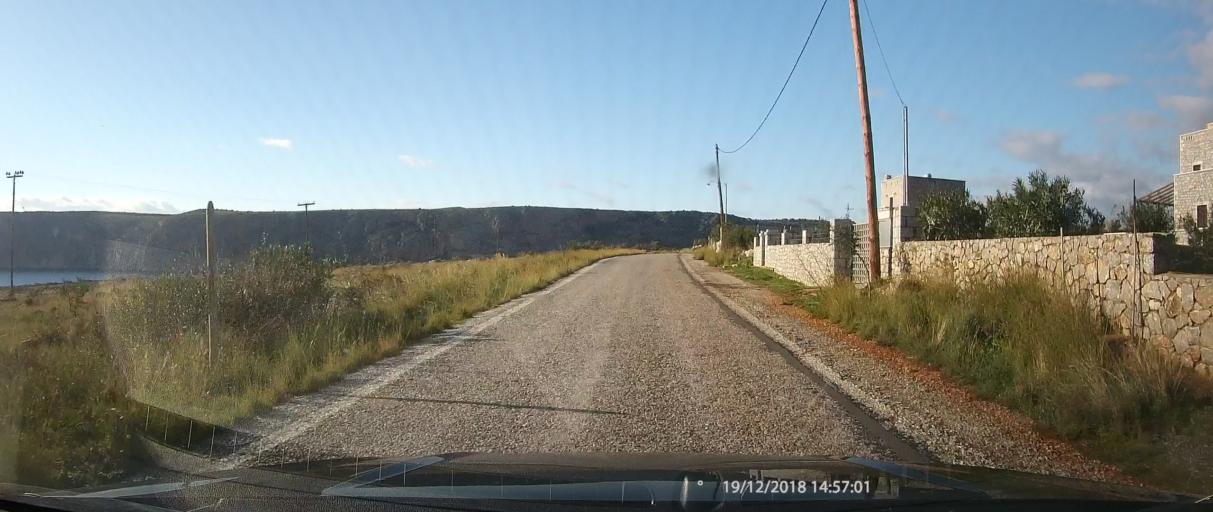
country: GR
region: Peloponnese
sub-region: Nomos Lakonias
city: Gytheio
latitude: 36.4794
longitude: 22.4109
